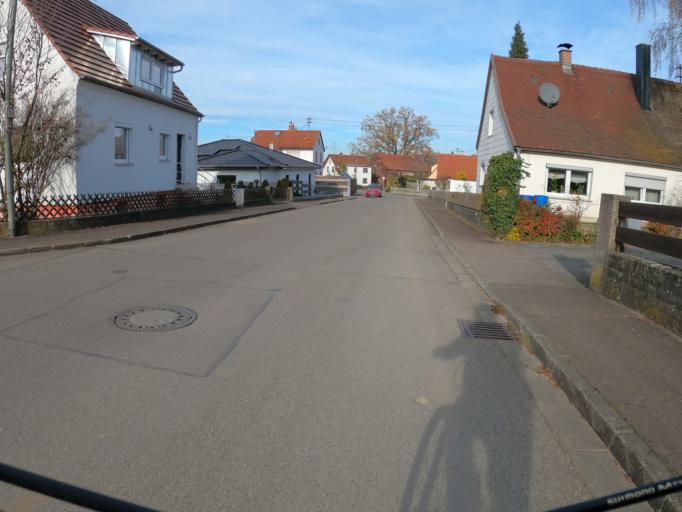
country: DE
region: Bavaria
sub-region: Swabia
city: Leipheim
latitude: 48.4210
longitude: 10.1865
